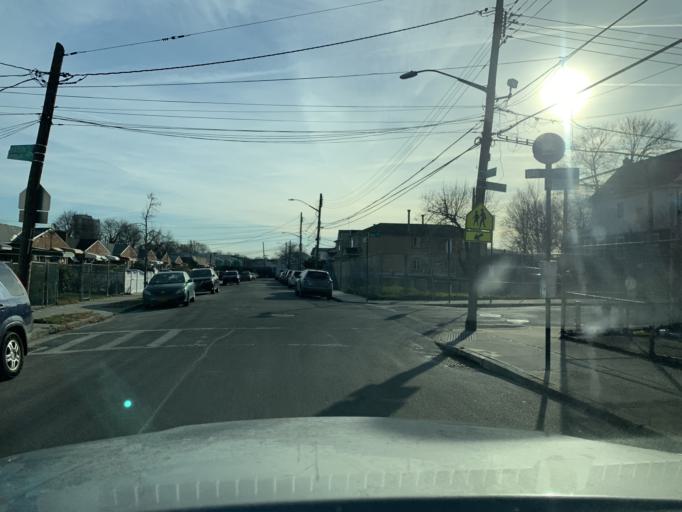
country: US
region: New York
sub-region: Queens County
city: Jamaica
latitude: 40.7009
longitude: -73.7813
